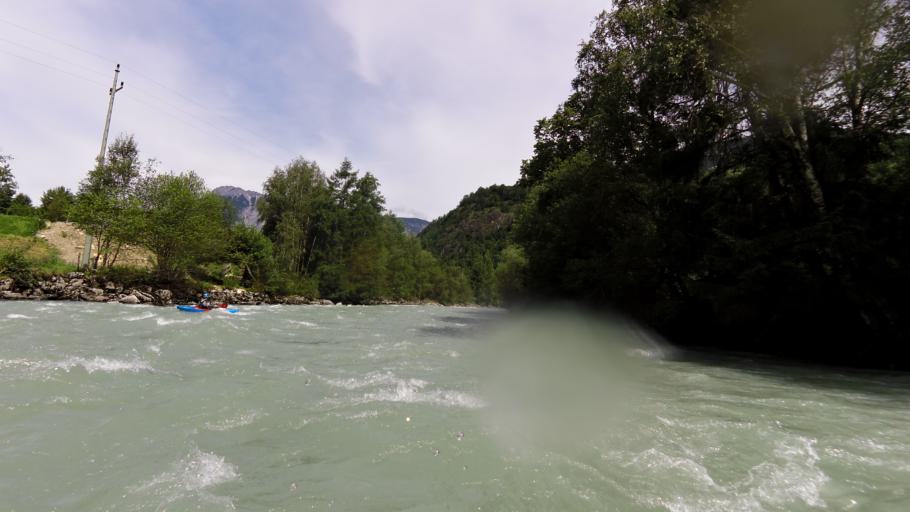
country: AT
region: Tyrol
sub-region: Politischer Bezirk Imst
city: Sautens
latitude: 47.2028
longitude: 10.8803
